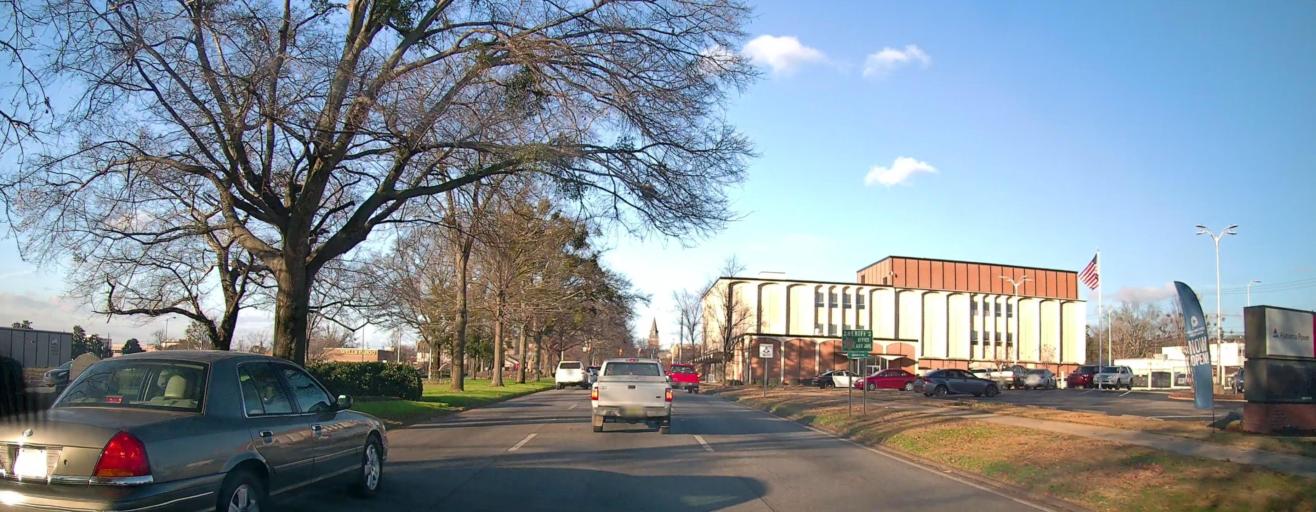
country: US
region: Alabama
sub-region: Calhoun County
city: Anniston
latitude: 33.6560
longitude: -85.8265
